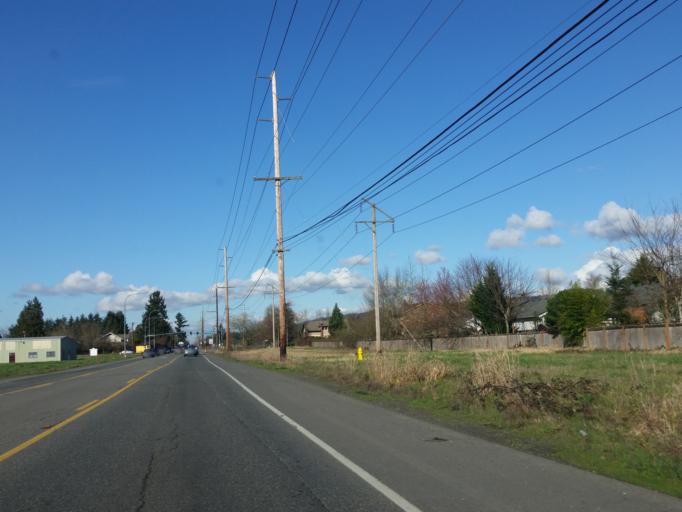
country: US
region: Washington
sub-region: Pierce County
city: Alderton
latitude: 47.1781
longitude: -122.2292
